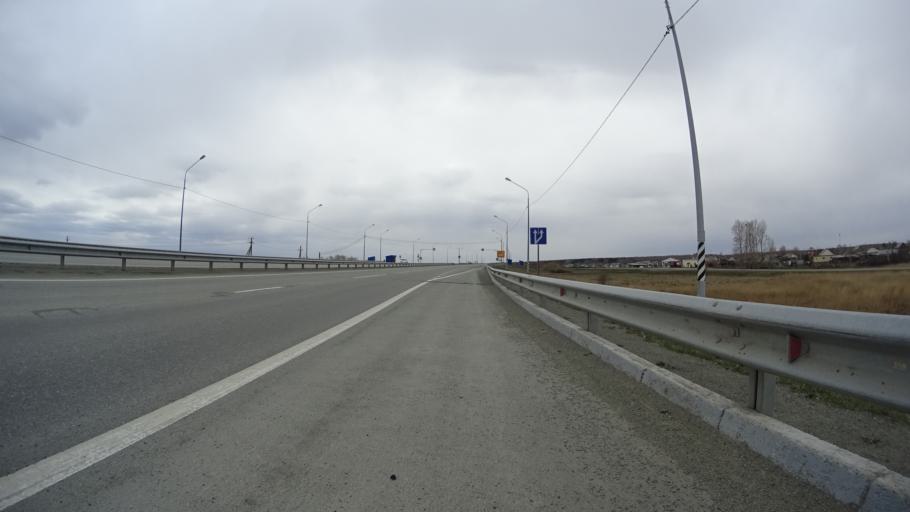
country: RU
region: Chelyabinsk
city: Yemanzhelinka
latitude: 54.7979
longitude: 61.3079
